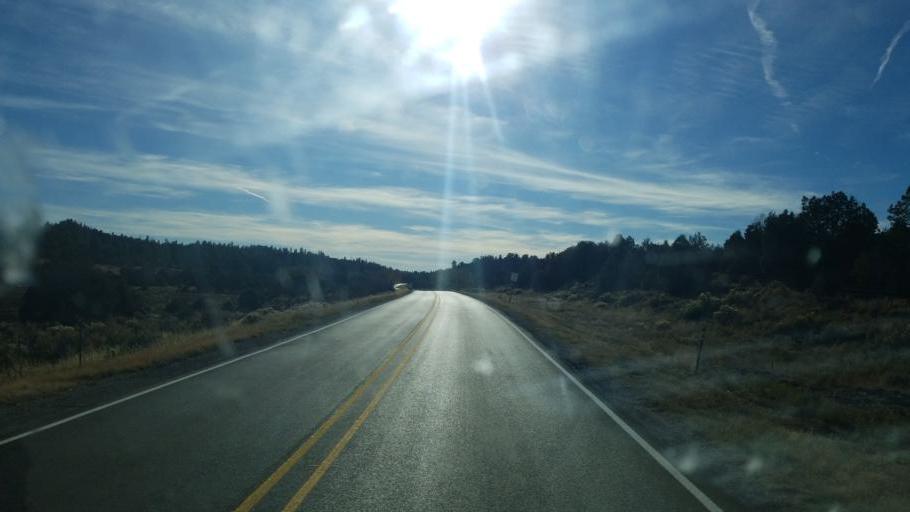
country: US
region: New Mexico
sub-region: Rio Arriba County
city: Dulce
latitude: 36.7950
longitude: -107.0417
